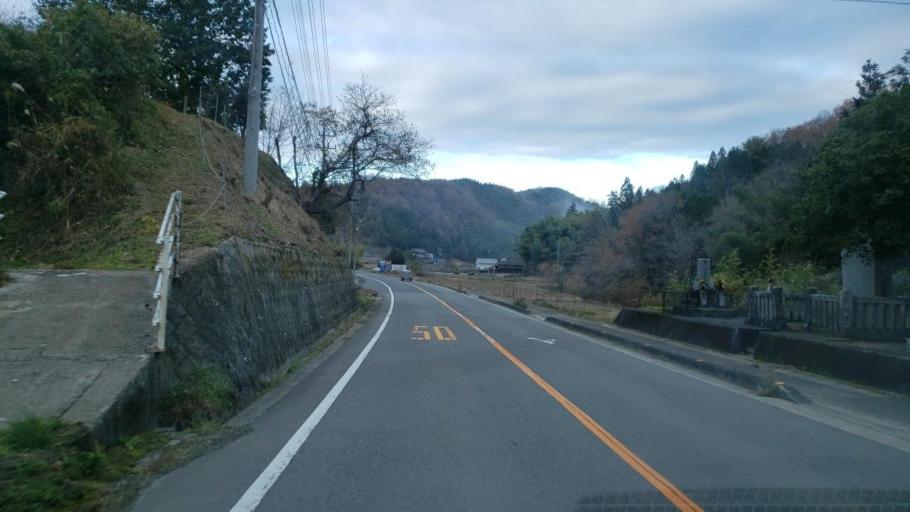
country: JP
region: Tokushima
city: Wakimachi
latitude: 34.1778
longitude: 134.1668
